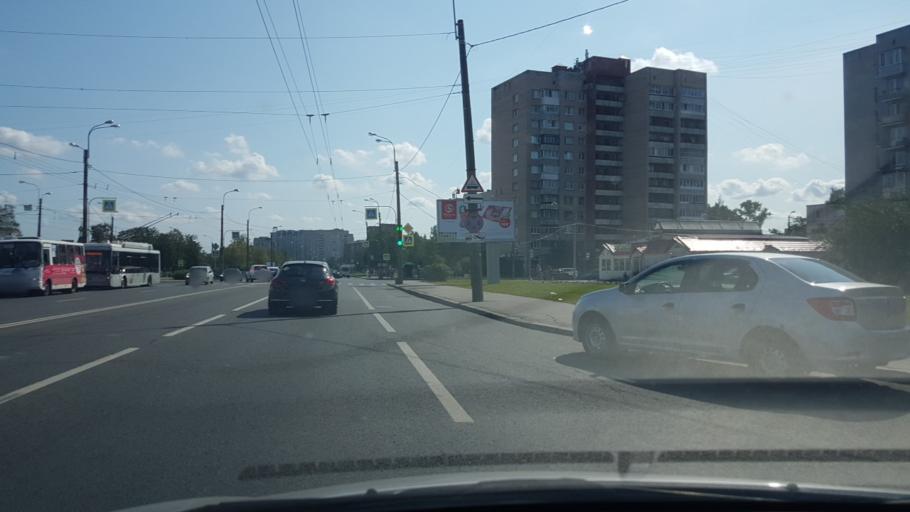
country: RU
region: St.-Petersburg
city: Sosnovaya Polyana
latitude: 59.8347
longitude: 30.1552
